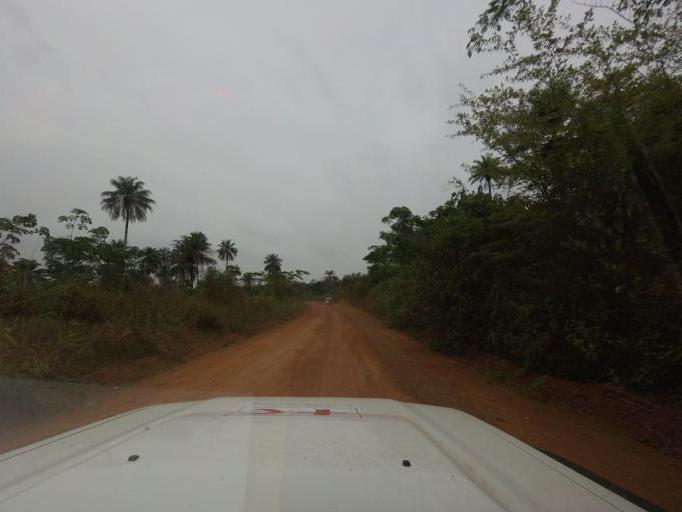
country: LR
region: Lofa
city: Voinjama
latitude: 8.4033
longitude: -9.7831
